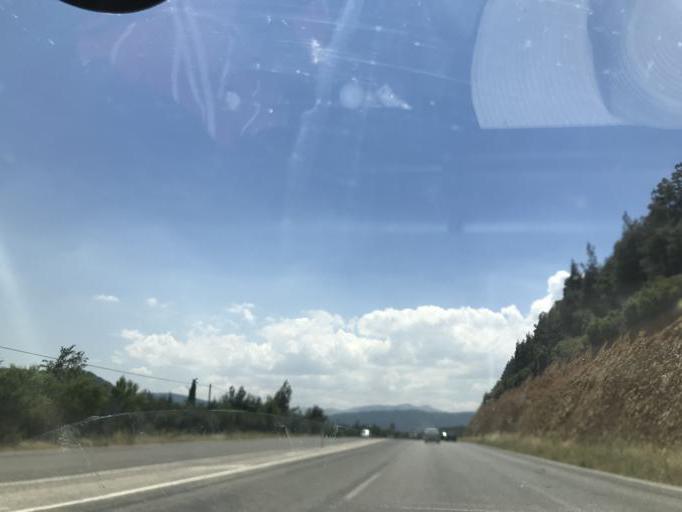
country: TR
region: Denizli
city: Honaz
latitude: 37.7191
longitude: 29.2083
